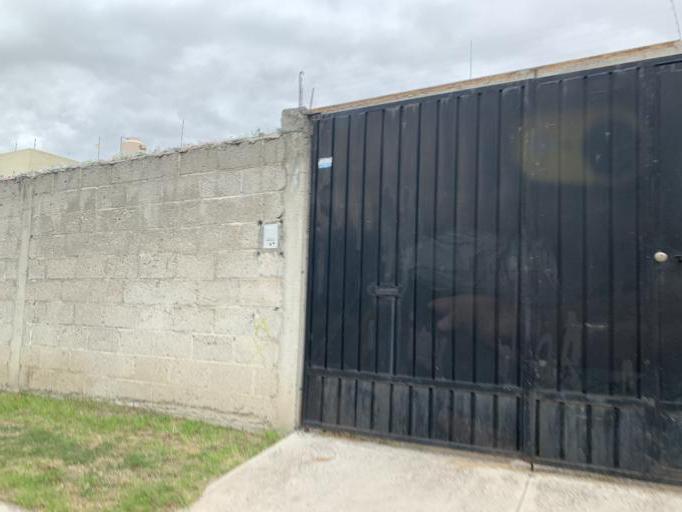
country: MX
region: Puebla
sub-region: Puebla
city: Articulo Primero Constitucional
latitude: 18.9932
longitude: -98.1946
